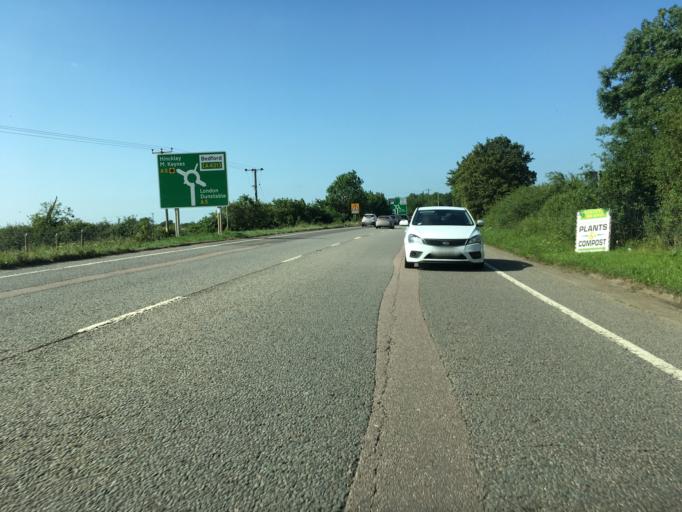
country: GB
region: England
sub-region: Milton Keynes
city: Water Eaton
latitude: 51.9894
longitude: -0.7013
